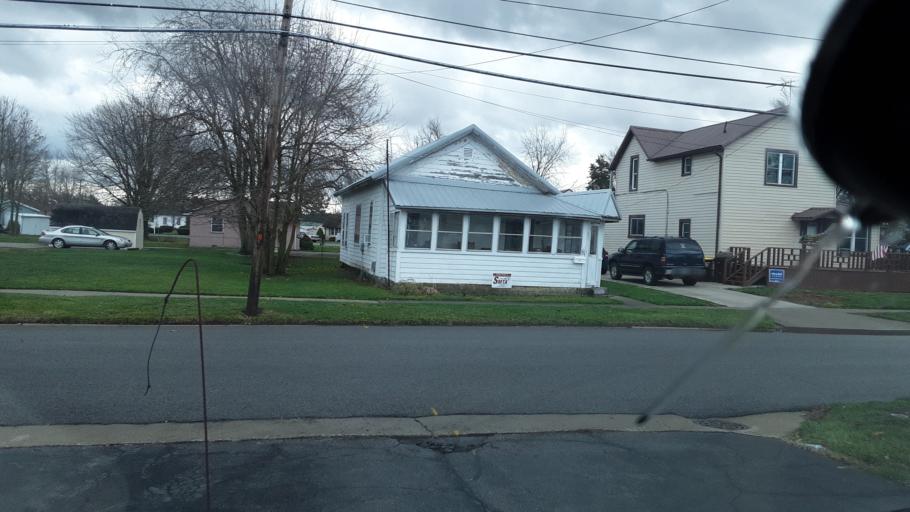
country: US
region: Ohio
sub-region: Defiance County
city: Hicksville
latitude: 41.2941
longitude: -84.7584
